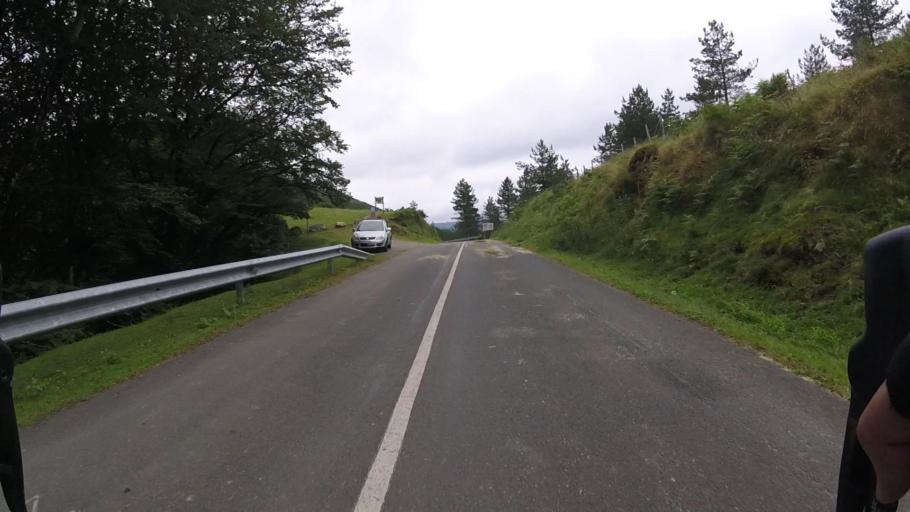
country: ES
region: Navarre
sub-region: Provincia de Navarra
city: Goizueta
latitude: 43.2455
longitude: -1.8128
